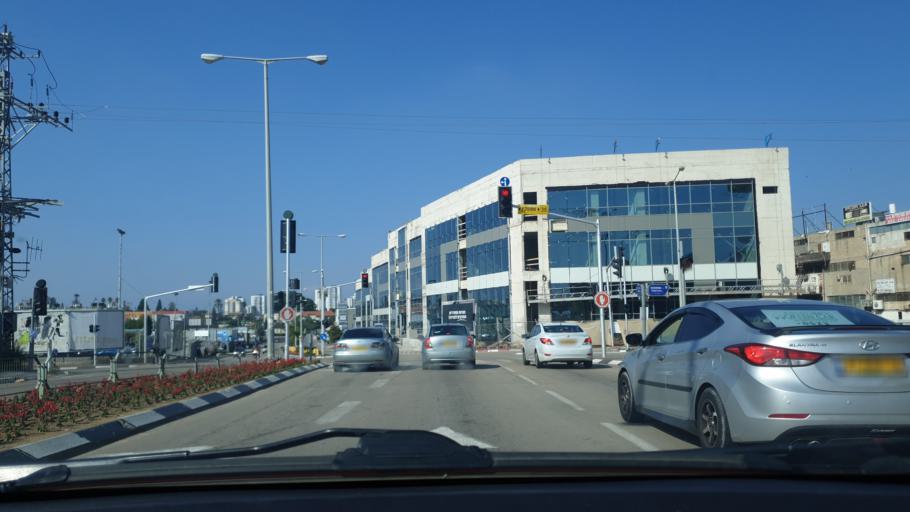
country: IL
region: Central District
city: Rishon LeZiyyon
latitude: 31.9760
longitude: 34.8118
